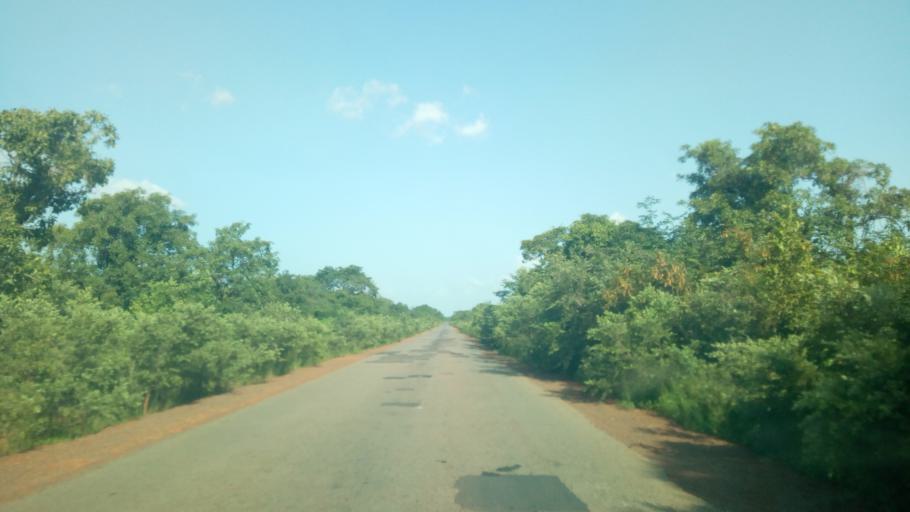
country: ML
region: Sikasso
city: Yorosso
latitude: 12.2113
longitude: -4.8918
